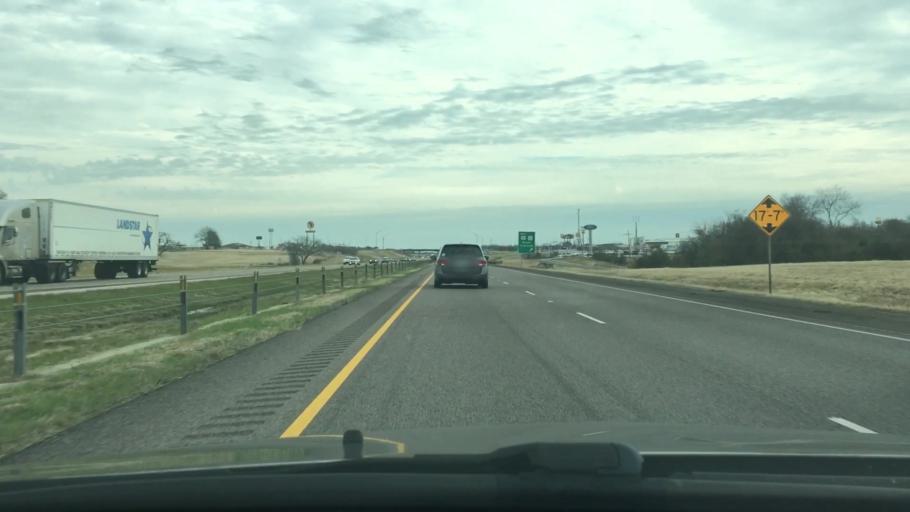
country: US
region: Texas
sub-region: Madison County
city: Madisonville
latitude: 30.9716
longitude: -95.8888
